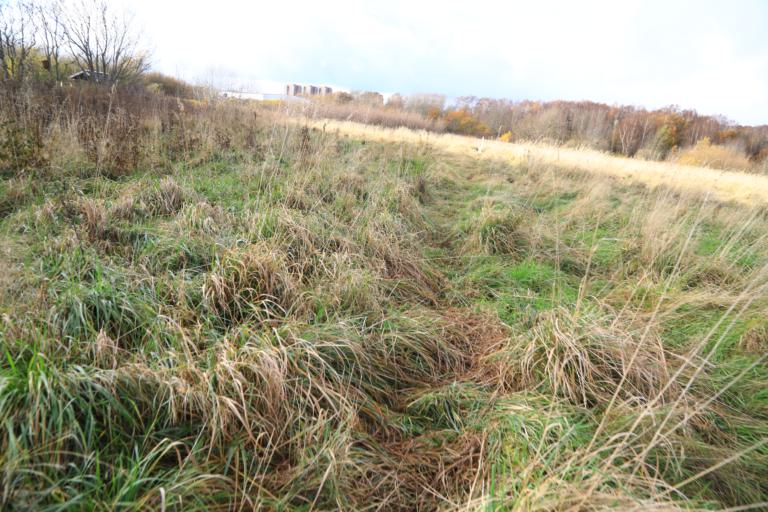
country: SE
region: Halland
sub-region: Varbergs Kommun
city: Traslovslage
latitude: 57.0892
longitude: 12.2805
